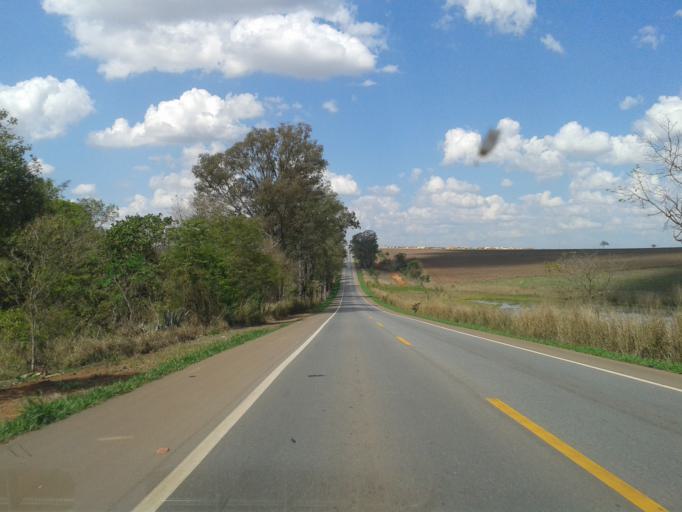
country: BR
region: Minas Gerais
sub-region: Luz
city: Luz
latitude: -19.7843
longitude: -45.7064
